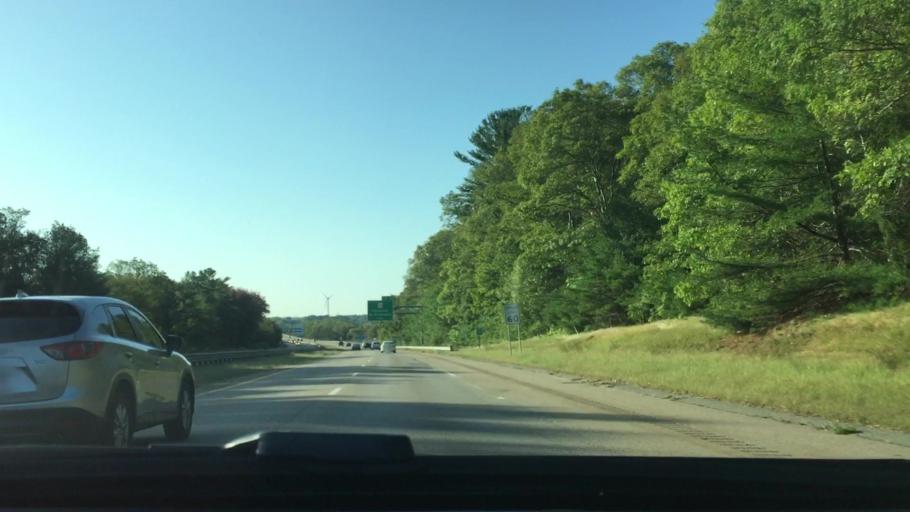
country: US
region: Massachusetts
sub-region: Plymouth County
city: Kingston
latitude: 42.0083
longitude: -70.7260
